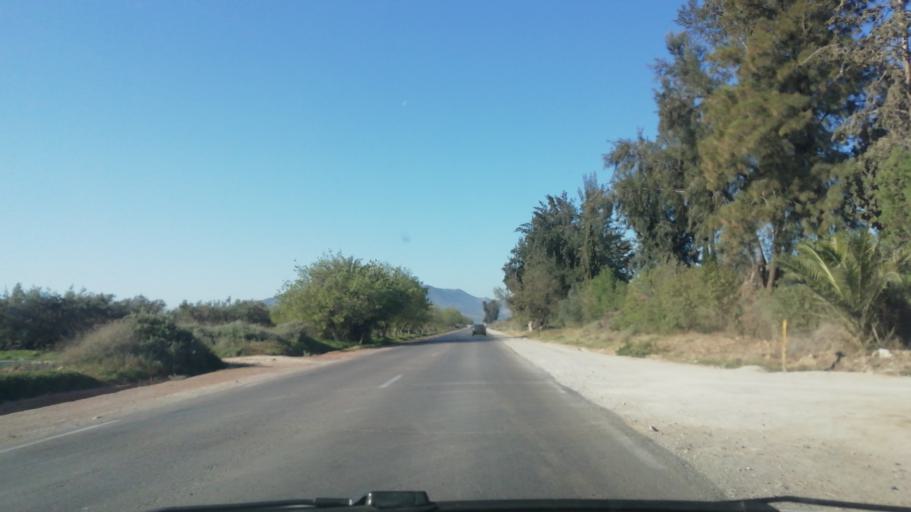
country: DZ
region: Mascara
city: Sig
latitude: 35.5444
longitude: -0.1241
